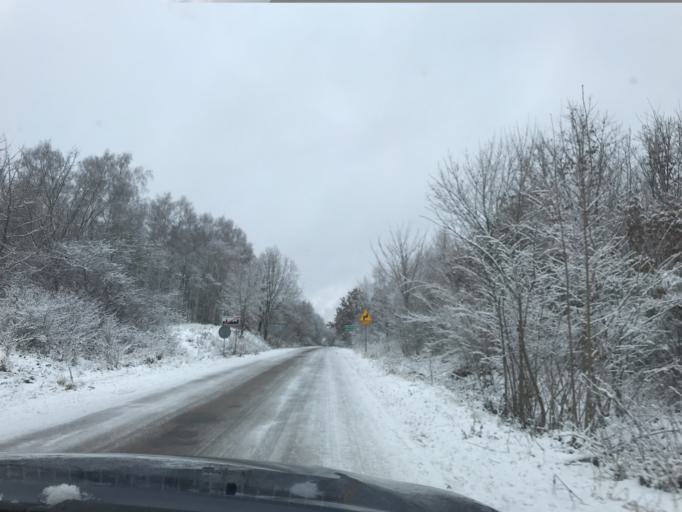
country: PL
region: Pomeranian Voivodeship
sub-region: Powiat bytowski
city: Bytow
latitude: 54.2219
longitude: 17.5640
